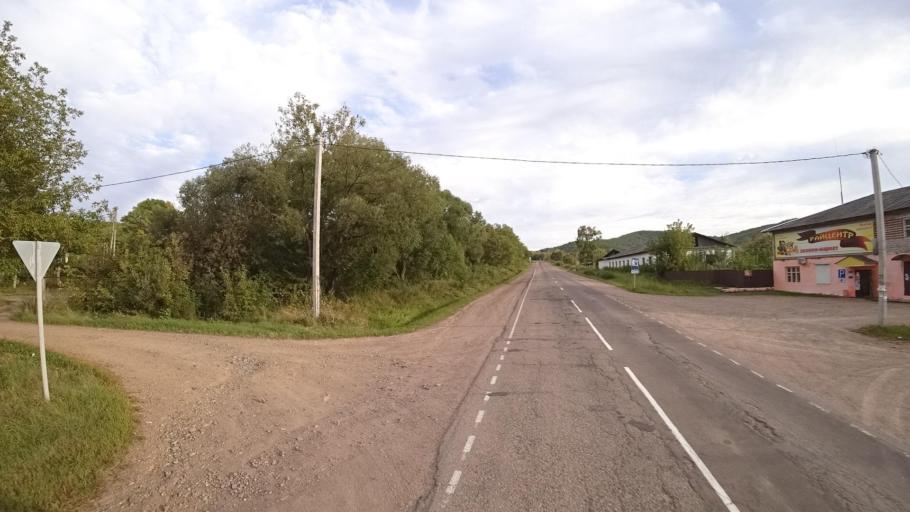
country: RU
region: Primorskiy
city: Yakovlevka
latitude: 44.4168
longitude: 133.4528
